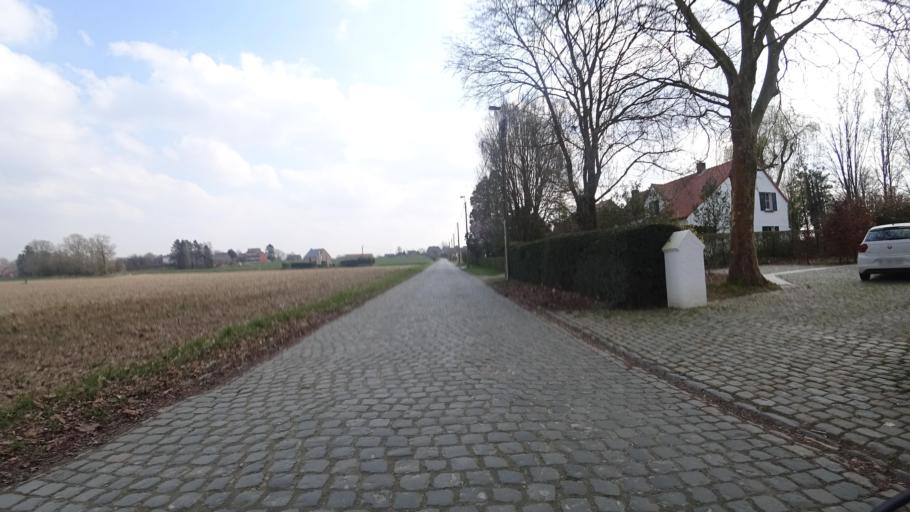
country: BE
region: Wallonia
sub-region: Province du Brabant Wallon
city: Walhain-Saint-Paul
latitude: 50.6145
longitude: 4.6846
